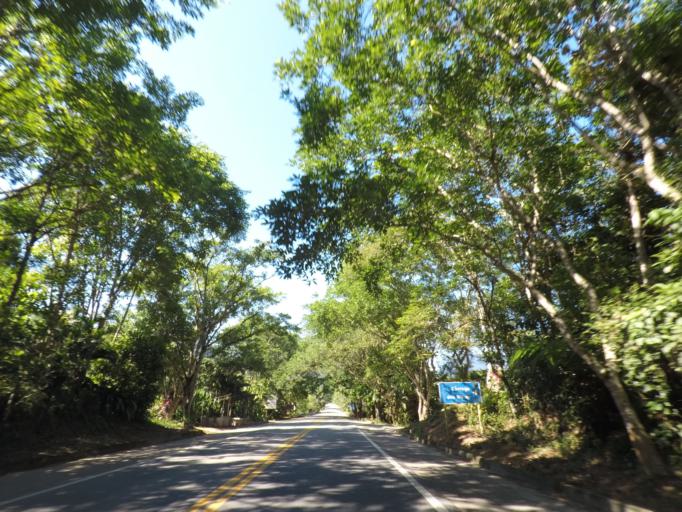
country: BR
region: Rio de Janeiro
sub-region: Parati
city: Paraty
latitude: -23.2936
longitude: -44.6988
